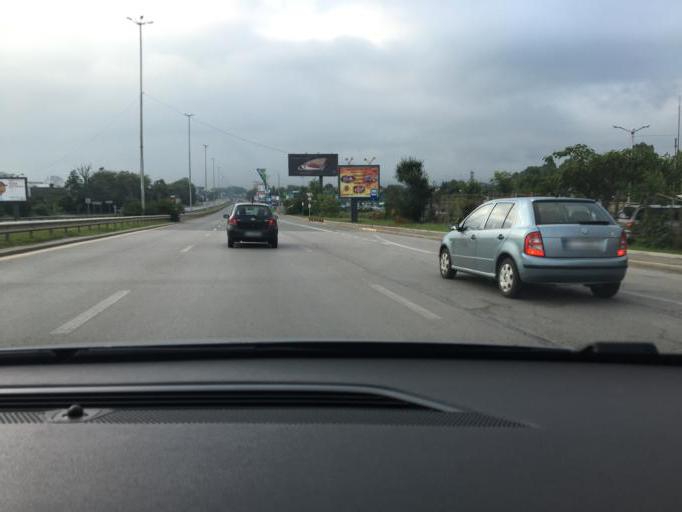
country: BG
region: Sofia-Capital
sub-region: Stolichna Obshtina
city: Sofia
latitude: 42.6429
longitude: 23.4022
